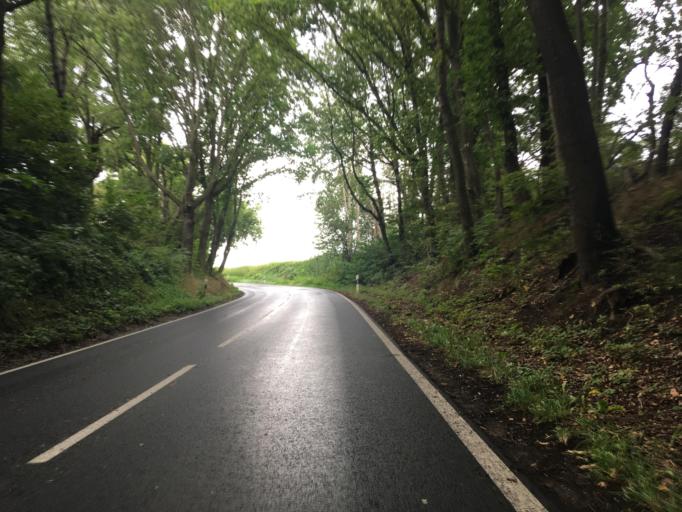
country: DE
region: Saxony
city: Dohma
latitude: 50.9304
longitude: 13.8974
